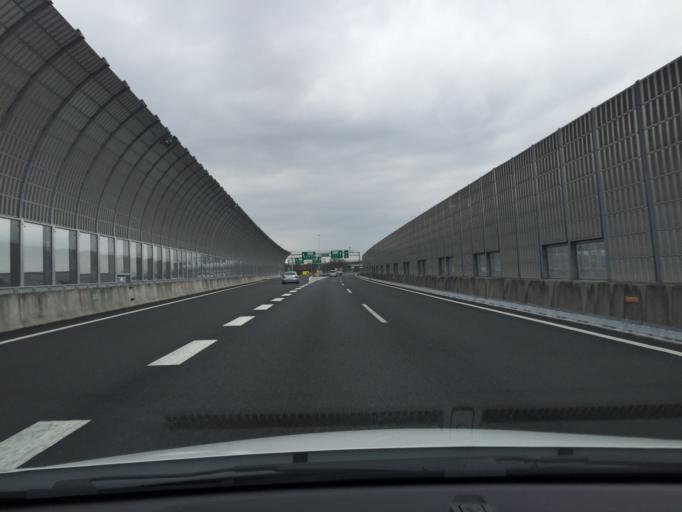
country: JP
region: Saitama
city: Sakado
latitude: 35.9358
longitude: 139.4069
